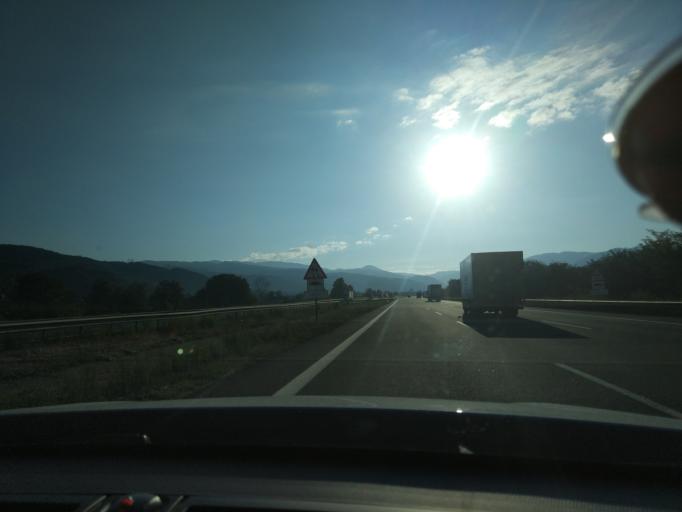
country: TR
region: Duzce
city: Kaynasli
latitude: 40.7827
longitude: 31.3113
